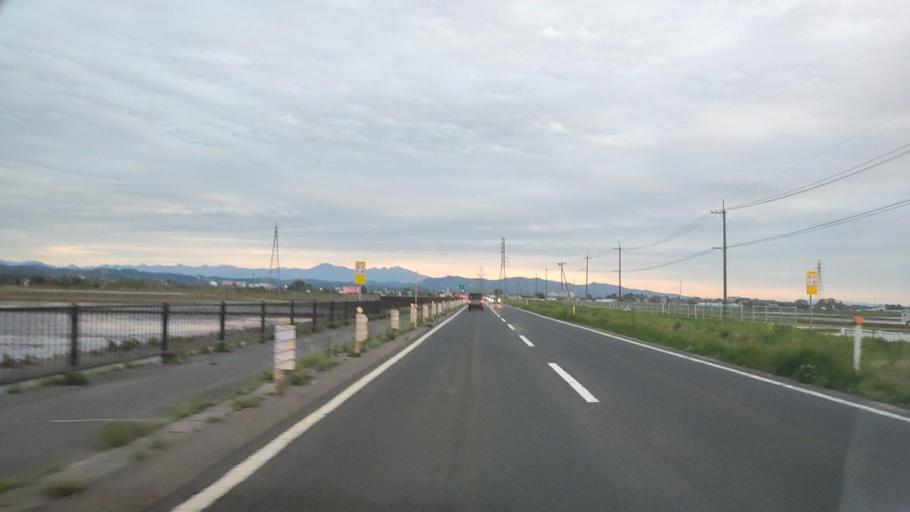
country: JP
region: Niigata
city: Niitsu-honcho
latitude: 37.8082
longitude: 139.1014
